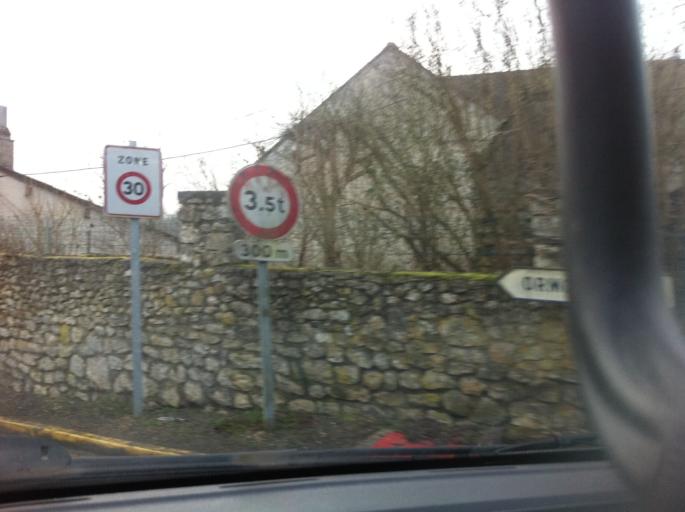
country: FR
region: Ile-de-France
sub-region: Departement de l'Essonne
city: Etampes
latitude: 48.4053
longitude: 2.1410
